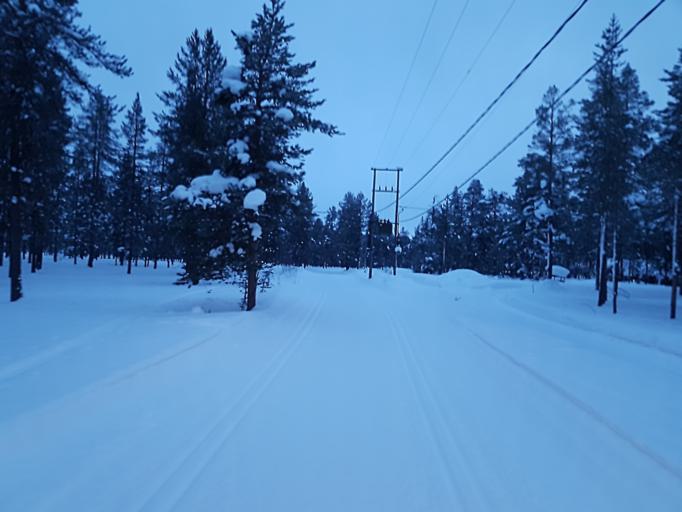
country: FI
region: Lapland
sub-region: Tunturi-Lappi
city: Kolari
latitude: 67.6222
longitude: 24.1731
